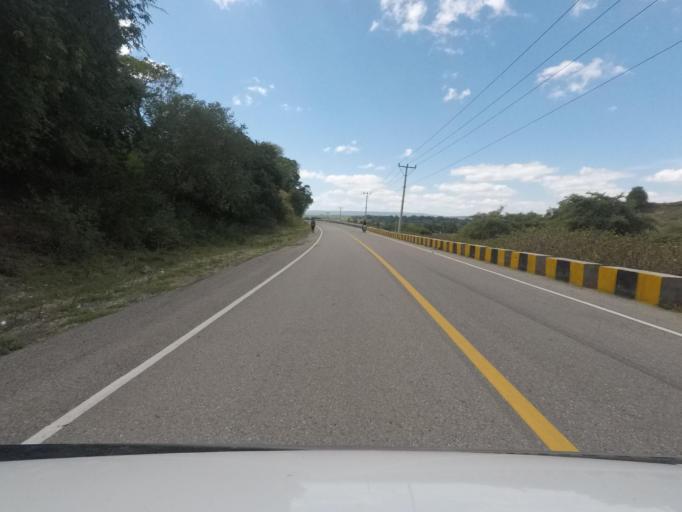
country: TL
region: Lautem
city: Lospalos
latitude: -8.4033
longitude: 126.8276
